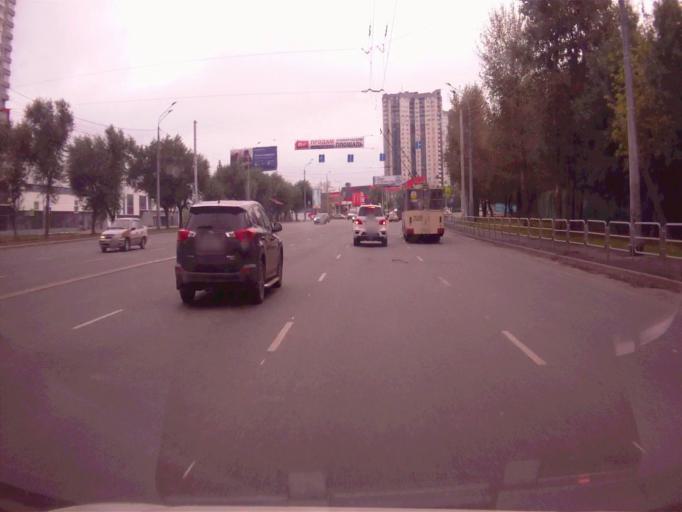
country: RU
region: Chelyabinsk
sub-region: Gorod Chelyabinsk
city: Chelyabinsk
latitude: 55.1709
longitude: 61.3677
